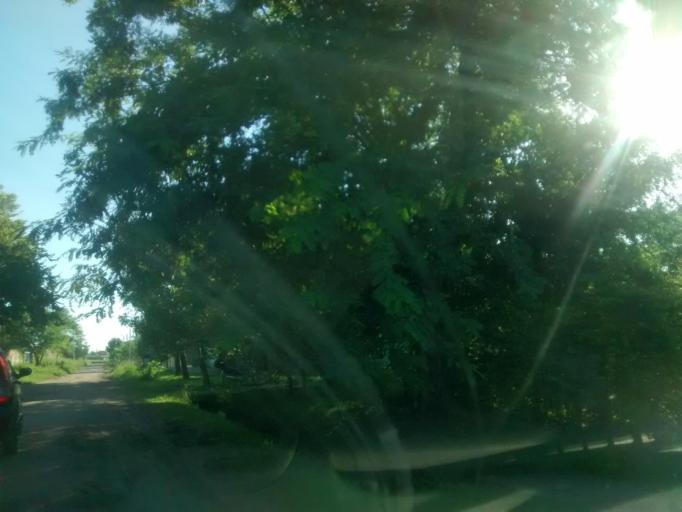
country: AR
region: Chaco
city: Fontana
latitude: -27.4612
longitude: -59.0366
